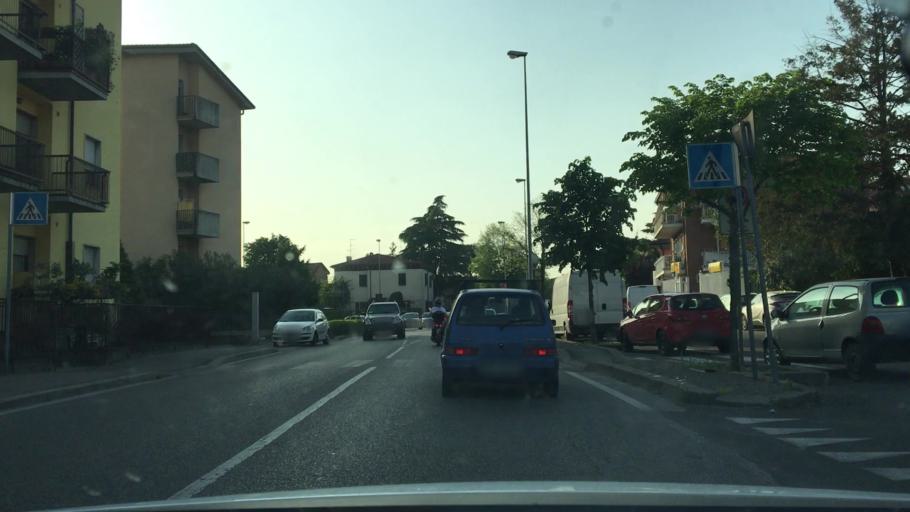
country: IT
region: Veneto
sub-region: Provincia di Verona
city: Verona
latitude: 45.4132
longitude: 10.9979
